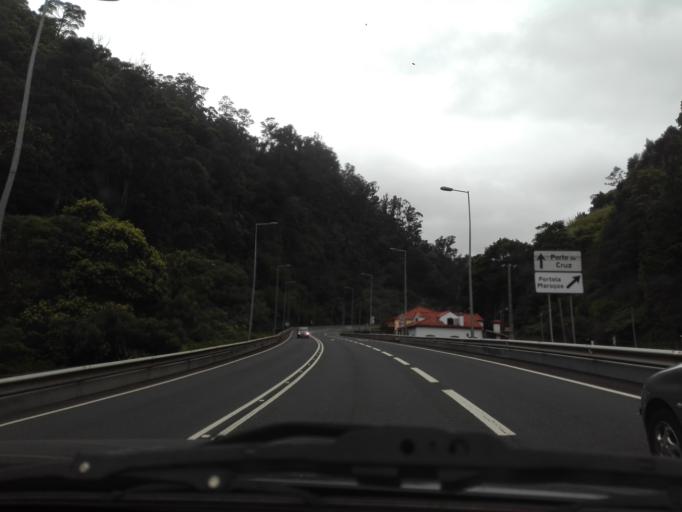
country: PT
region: Madeira
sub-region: Machico
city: Machico
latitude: 32.7349
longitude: -16.8036
